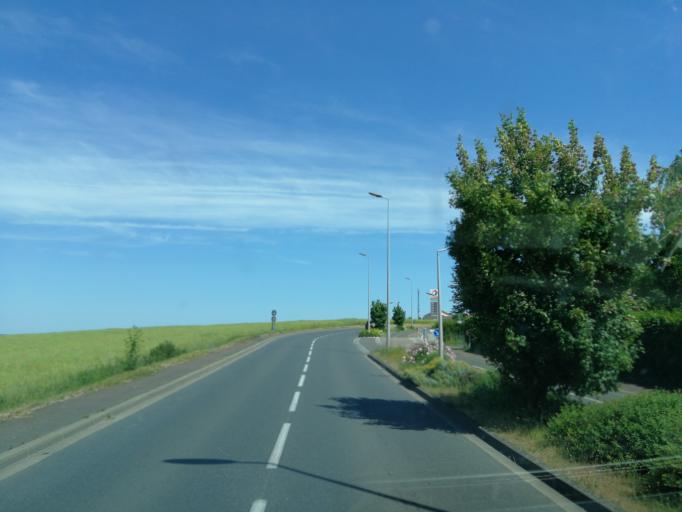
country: FR
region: Poitou-Charentes
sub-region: Departement des Deux-Sevres
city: Saint-Jean-de-Thouars
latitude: 46.9760
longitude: -0.1931
